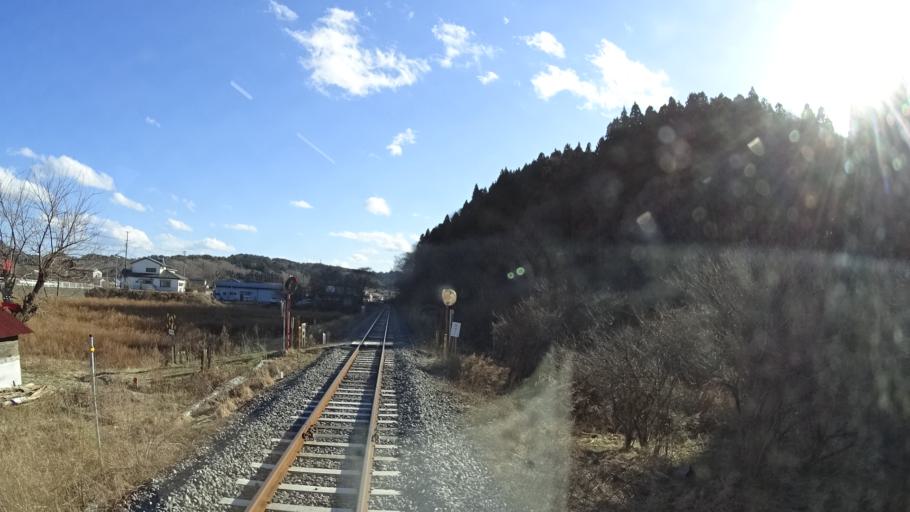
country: JP
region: Iwate
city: Miyako
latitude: 39.5699
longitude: 141.9321
